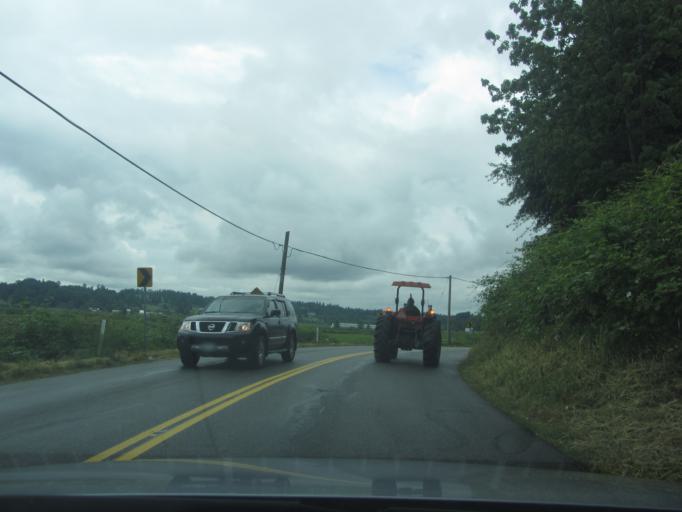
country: CA
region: British Columbia
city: Abbotsford
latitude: 49.1028
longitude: -122.3527
